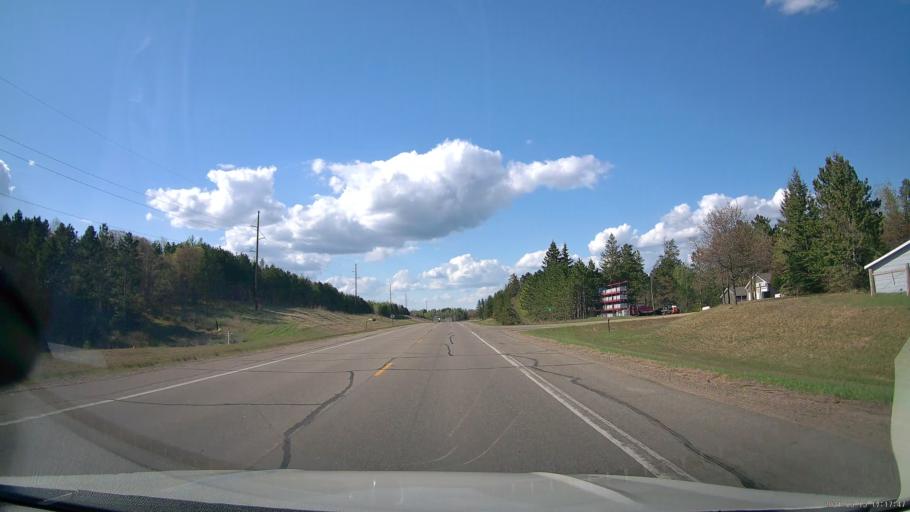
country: US
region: Minnesota
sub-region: Hubbard County
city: Park Rapids
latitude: 46.9502
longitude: -95.0156
